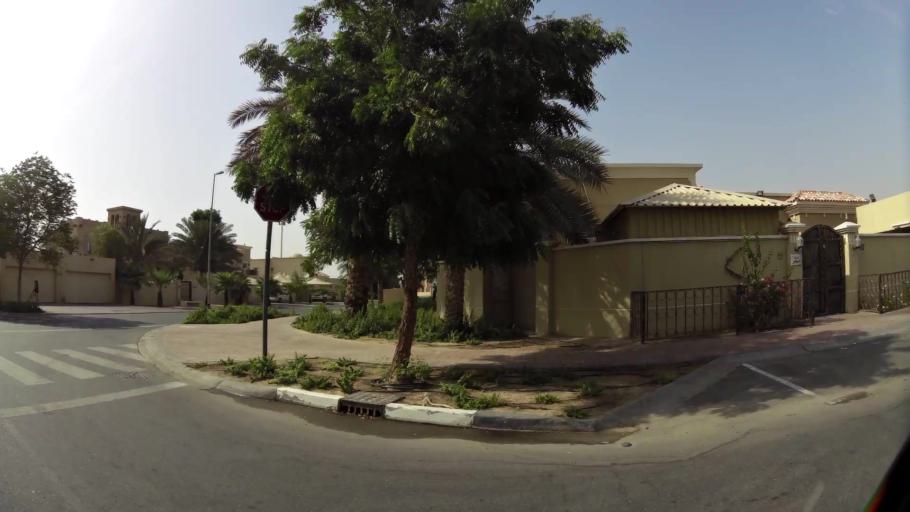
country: AE
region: Ash Shariqah
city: Sharjah
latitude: 25.2683
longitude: 55.4554
